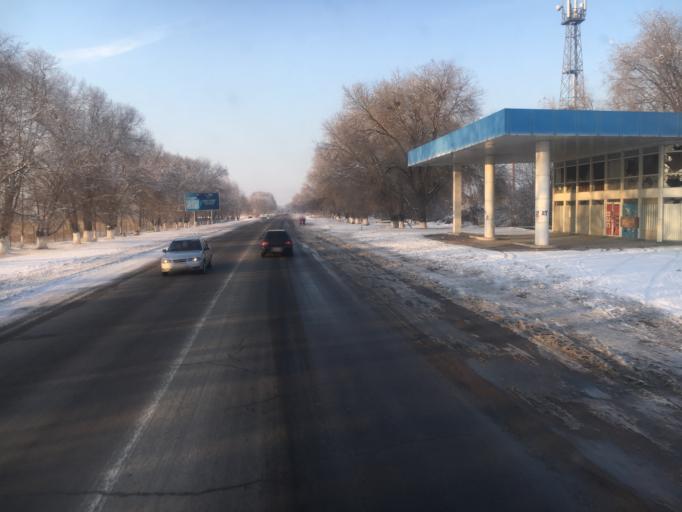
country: KZ
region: Almaty Oblysy
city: Burunday
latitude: 43.3351
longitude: 76.6605
